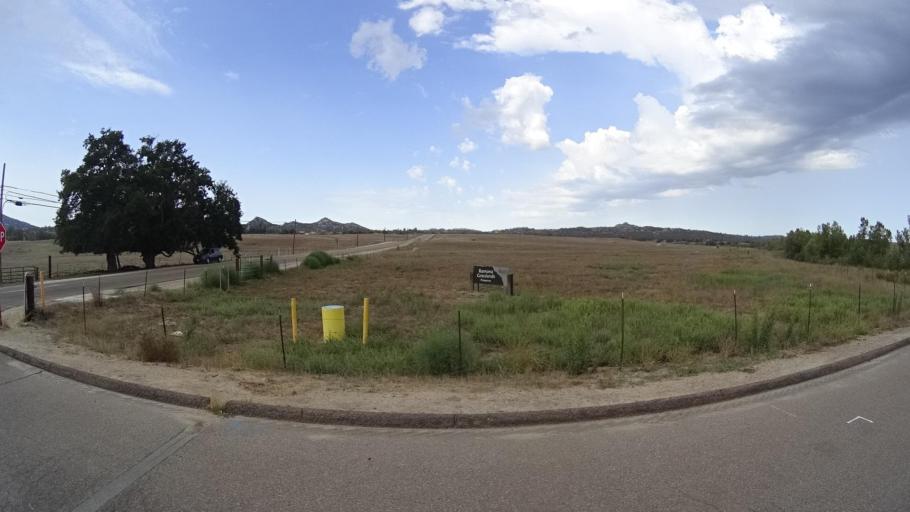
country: US
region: California
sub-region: San Diego County
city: San Pasqual
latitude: 33.0332
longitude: -116.9361
